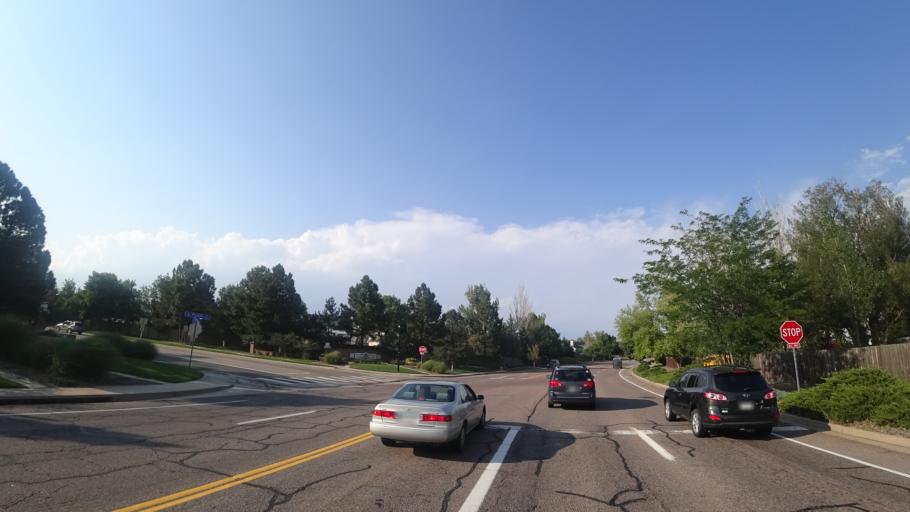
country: US
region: Colorado
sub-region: Arapahoe County
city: Dove Valley
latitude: 39.6143
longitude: -104.7443
